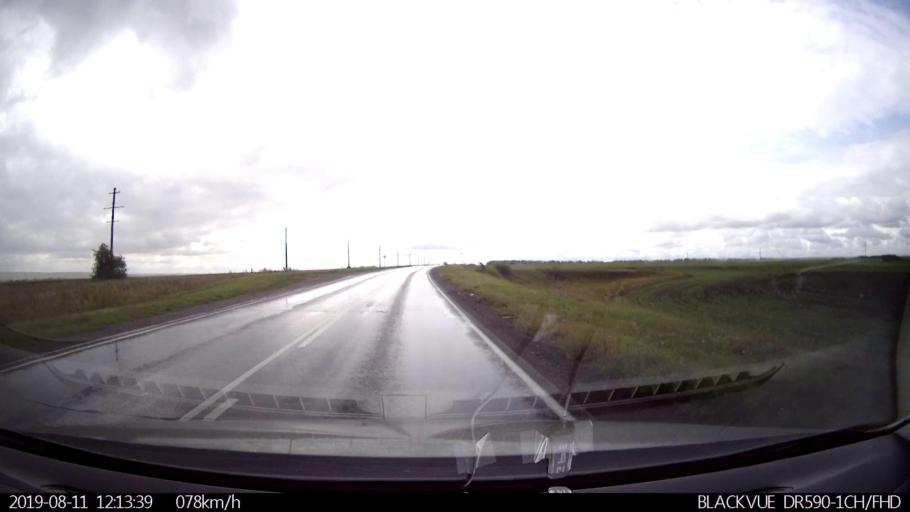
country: RU
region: Ulyanovsk
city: Ignatovka
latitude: 53.9598
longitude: 47.9901
